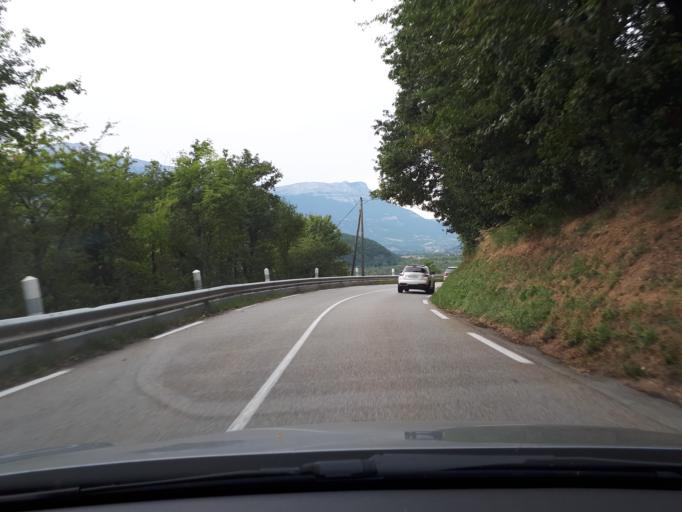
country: FR
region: Rhone-Alpes
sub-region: Departement de l'Isere
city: Saint-Georges-de-Commiers
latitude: 45.0410
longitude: 5.7055
